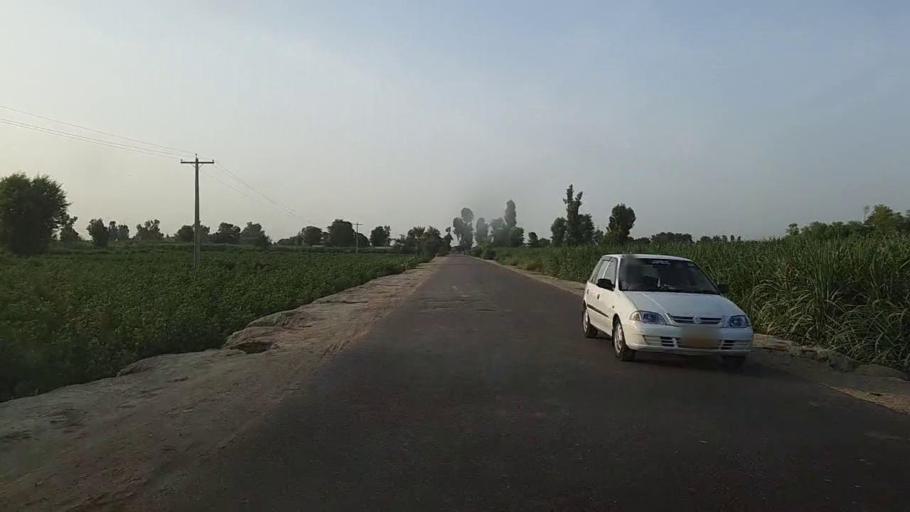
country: PK
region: Sindh
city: Ubauro
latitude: 28.1863
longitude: 69.8278
